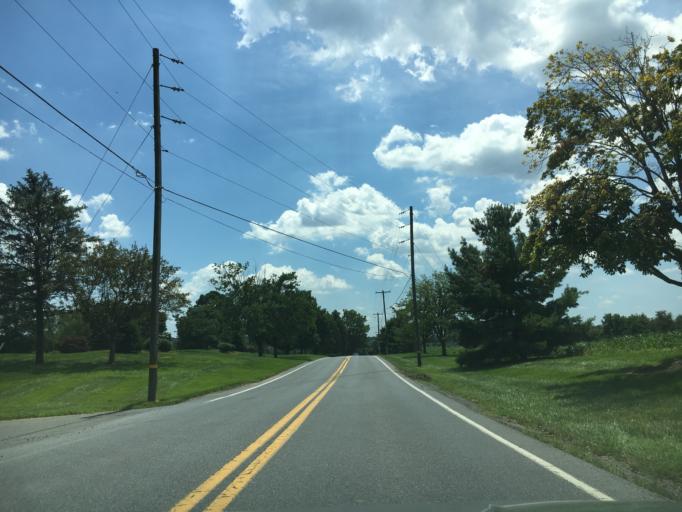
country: US
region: Pennsylvania
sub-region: Lehigh County
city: Schnecksville
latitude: 40.6412
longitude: -75.5779
